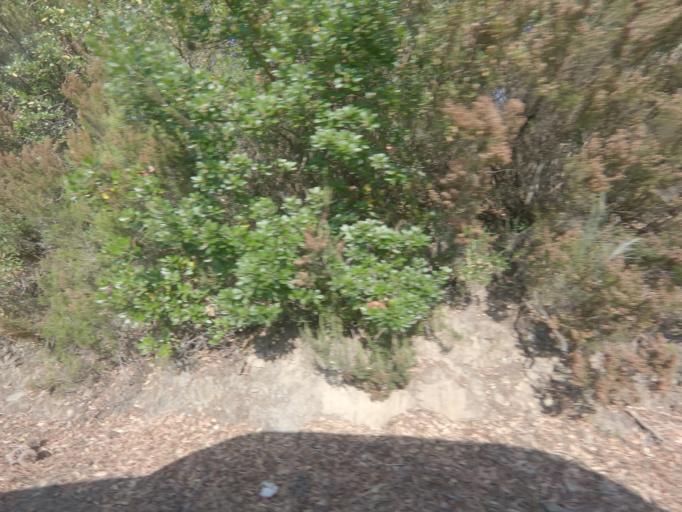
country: PT
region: Vila Real
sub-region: Sabrosa
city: Vilela
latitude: 41.1779
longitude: -7.5974
